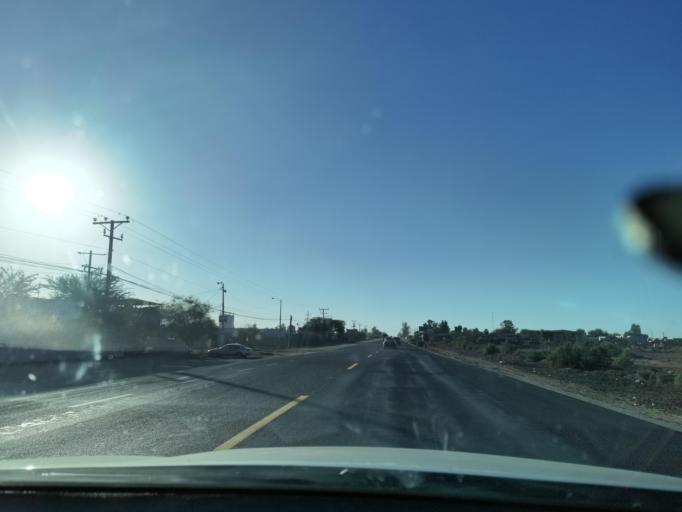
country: MX
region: Baja California
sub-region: Mexicali
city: Islas Agrarias Grupo A
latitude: 32.6484
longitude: -115.3322
